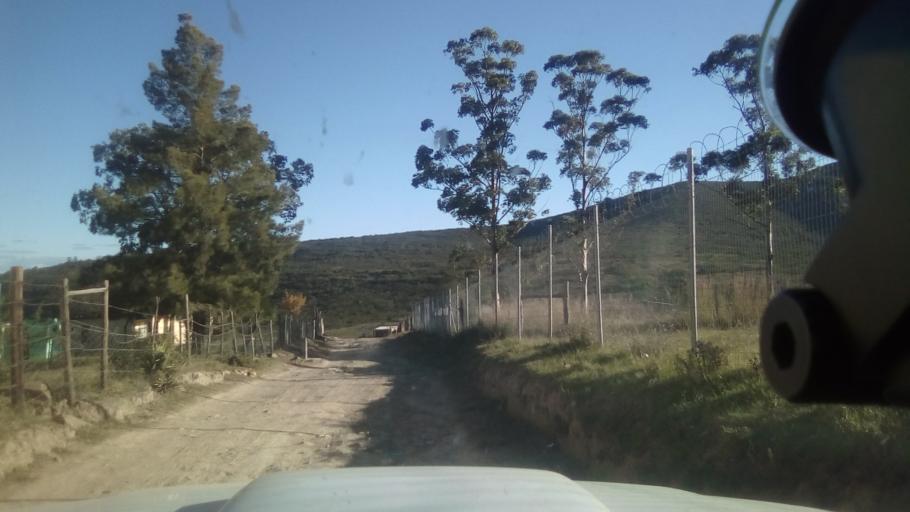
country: ZA
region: Eastern Cape
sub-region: Buffalo City Metropolitan Municipality
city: Bhisho
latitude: -32.7341
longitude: 27.3608
